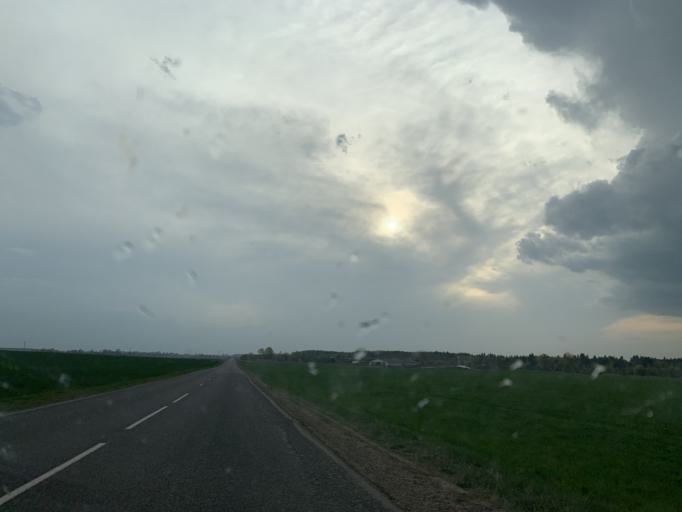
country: BY
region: Minsk
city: Kapyl'
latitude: 53.3050
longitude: 27.0729
